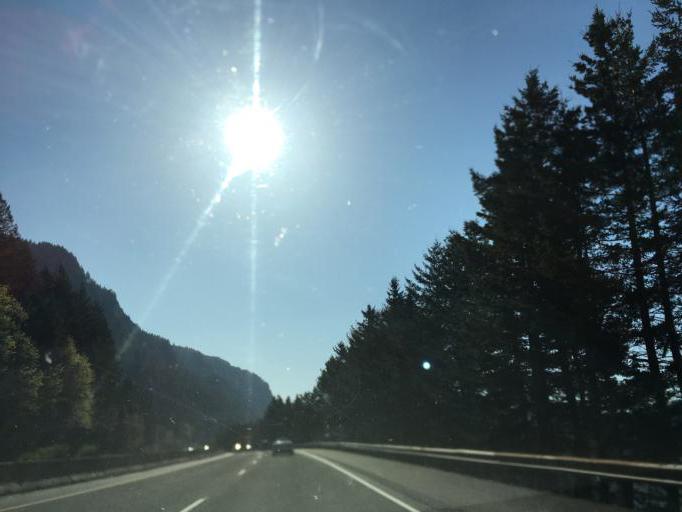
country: US
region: Oregon
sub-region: Hood River County
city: Cascade Locks
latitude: 45.5841
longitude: -122.0957
